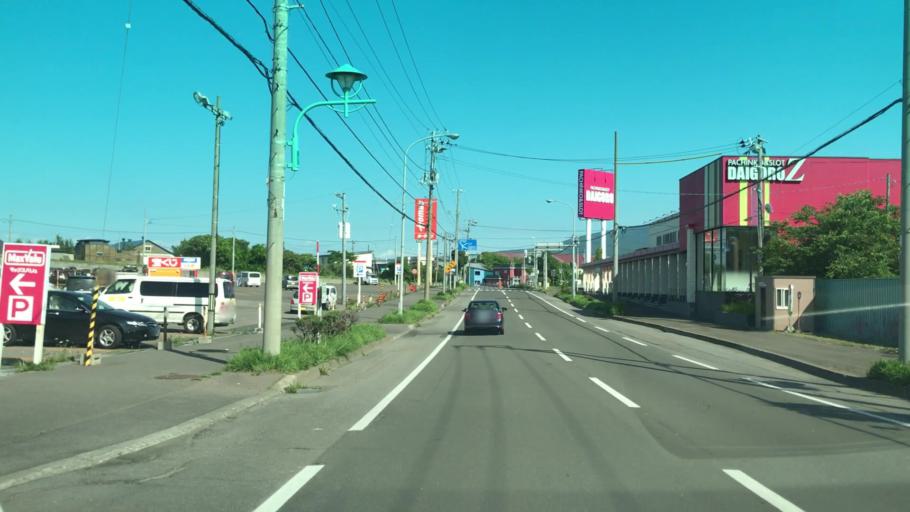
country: JP
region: Hokkaido
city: Iwanai
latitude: 42.9819
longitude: 140.5380
